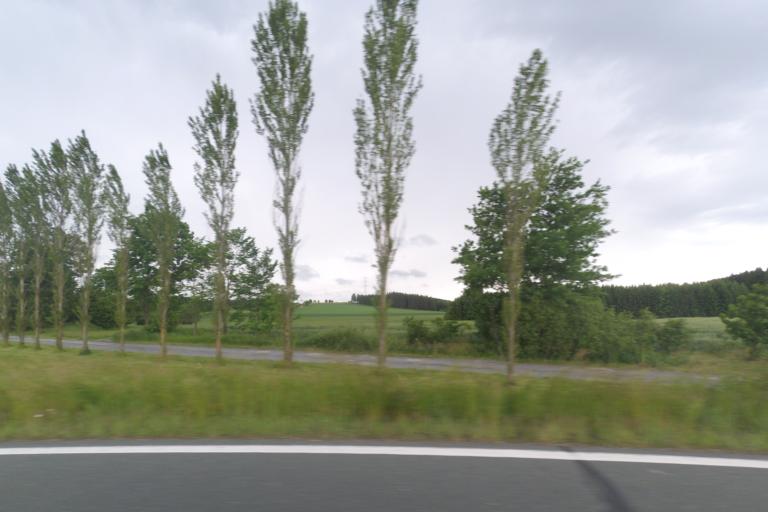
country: DE
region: Bavaria
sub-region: Upper Franconia
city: Helmbrechts
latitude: 50.2104
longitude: 11.7279
